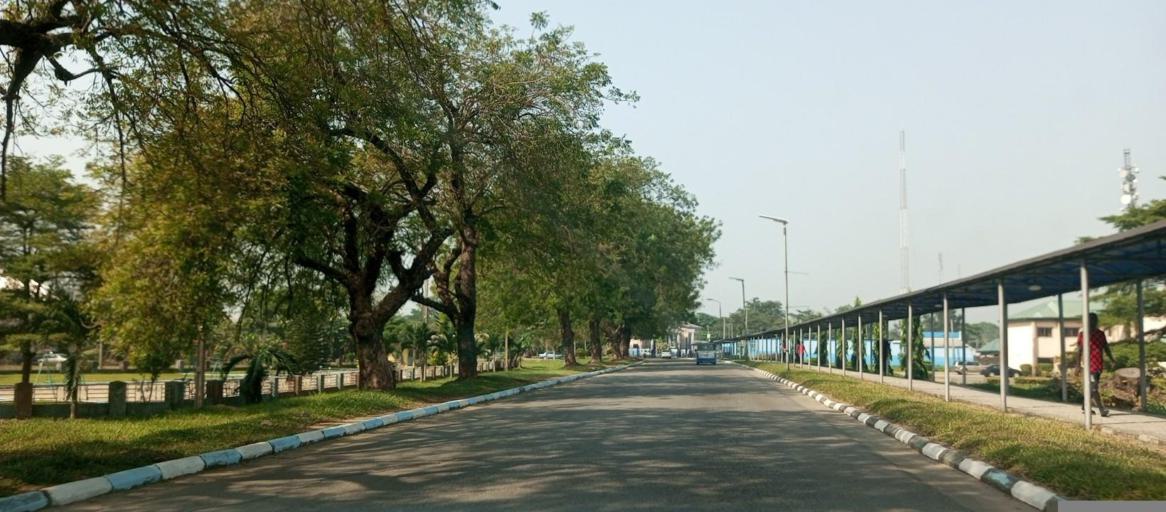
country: NG
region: Rivers
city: Emuoha
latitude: 4.9022
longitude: 6.9082
